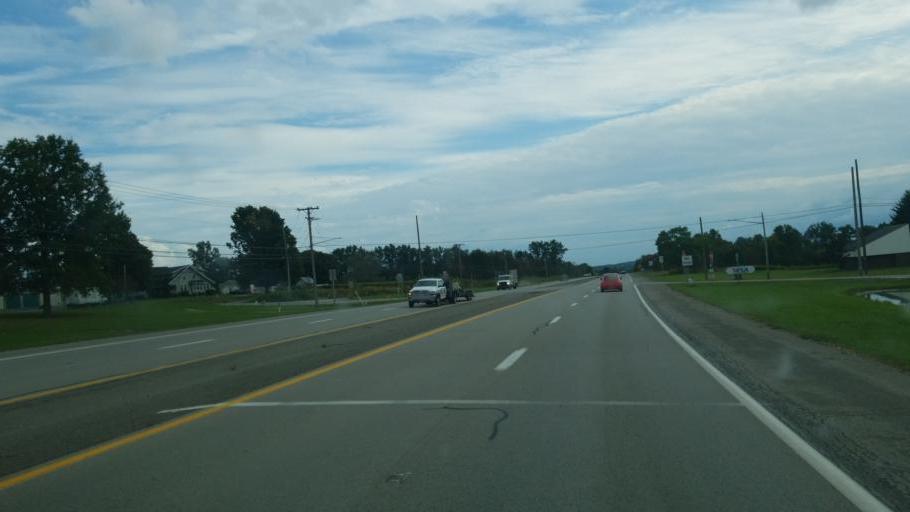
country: US
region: Pennsylvania
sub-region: Mercer County
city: Reynolds Heights
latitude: 41.3201
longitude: -80.4113
